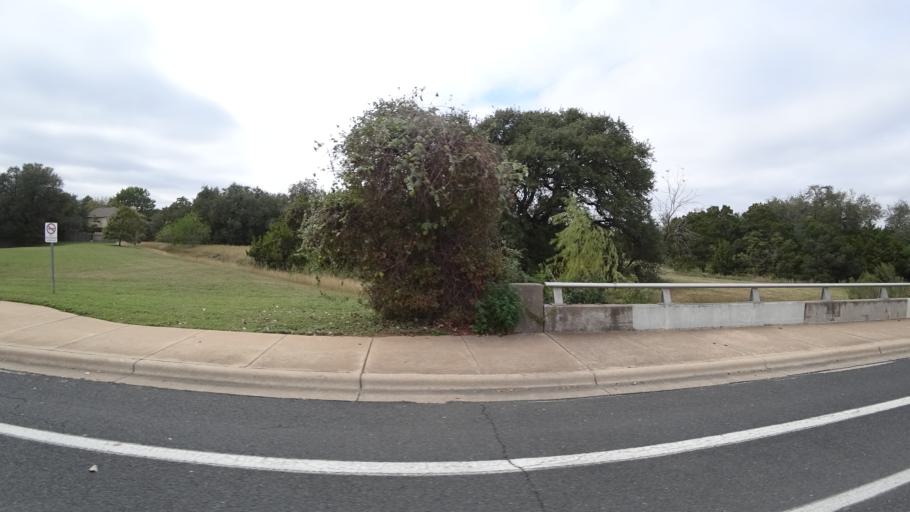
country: US
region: Texas
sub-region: Travis County
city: Shady Hollow
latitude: 30.2226
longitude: -97.8731
